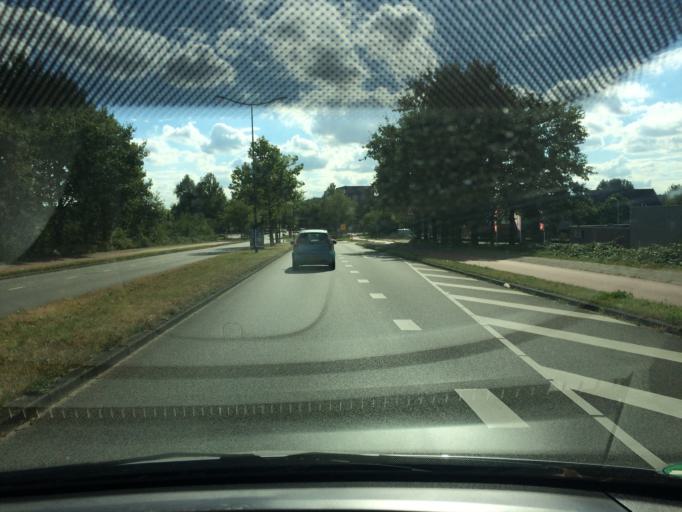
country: NL
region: North Brabant
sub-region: Gemeente Breda
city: Hoge Vucht
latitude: 51.5954
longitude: 4.7990
